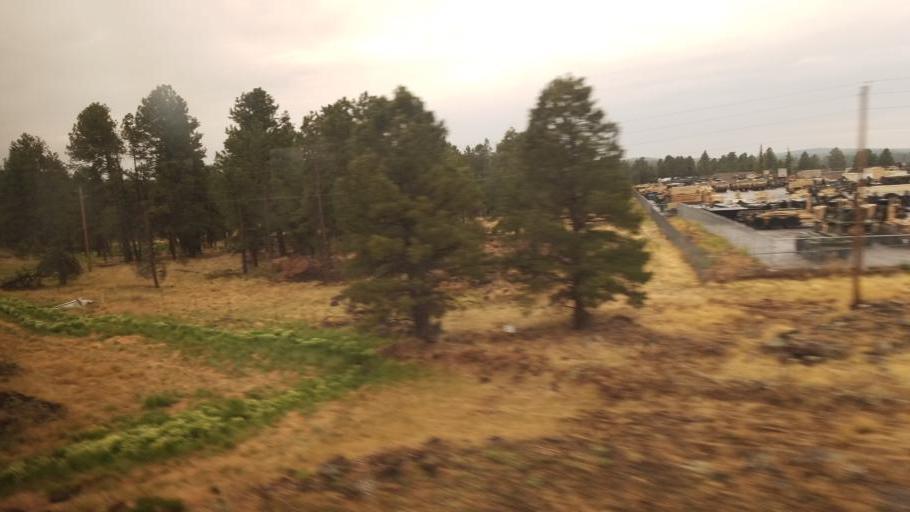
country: US
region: Arizona
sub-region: Coconino County
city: Parks
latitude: 35.2293
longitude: -111.8131
